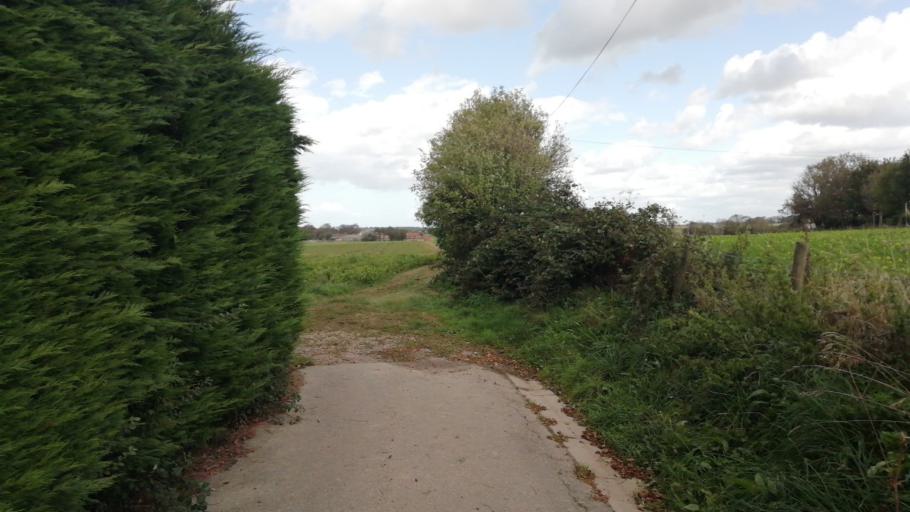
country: FR
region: Haute-Normandie
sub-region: Departement de la Seine-Maritime
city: Saint-Jouin-Bruneval
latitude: 49.6522
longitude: 0.1910
